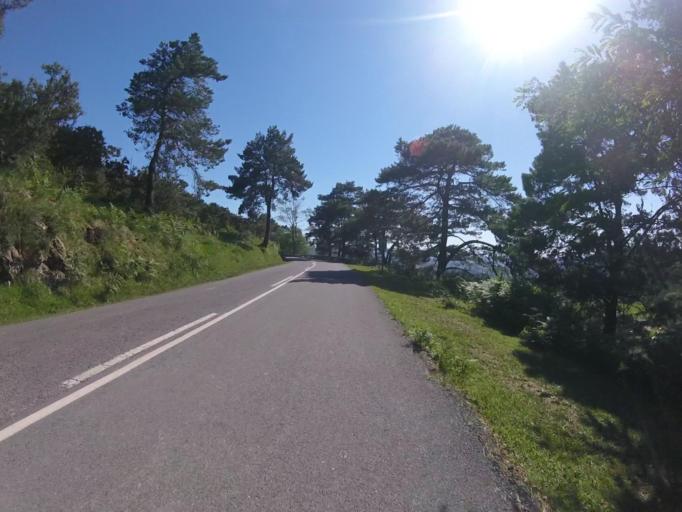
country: ES
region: Basque Country
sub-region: Provincia de Guipuzcoa
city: Irun
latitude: 43.2994
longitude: -1.8222
